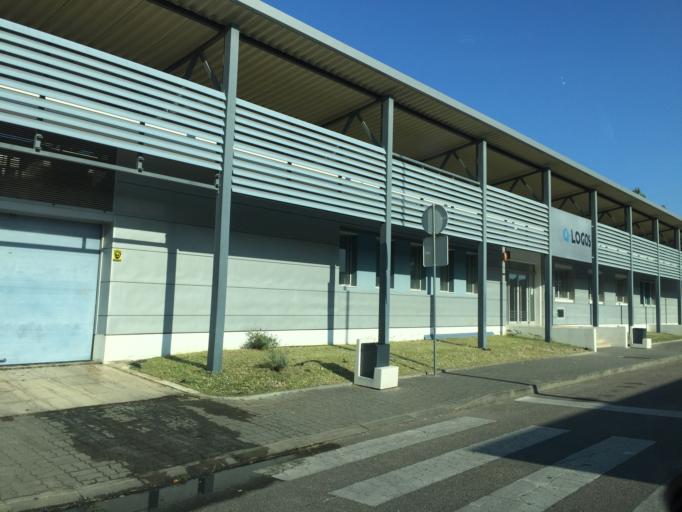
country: PT
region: Santarem
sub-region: Abrantes
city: Abrantes
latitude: 39.4746
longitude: -8.1887
